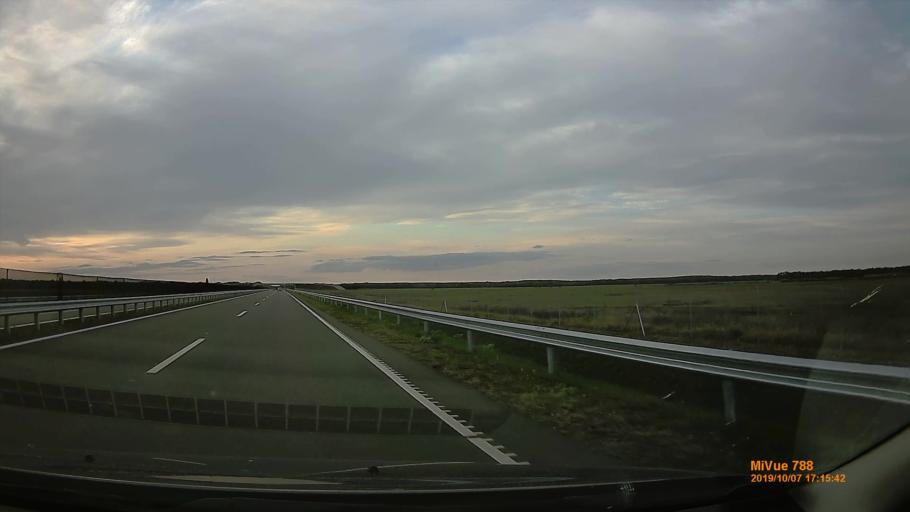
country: HU
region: Jasz-Nagykun-Szolnok
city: Kunszentmarton
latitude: 46.8490
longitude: 20.3236
